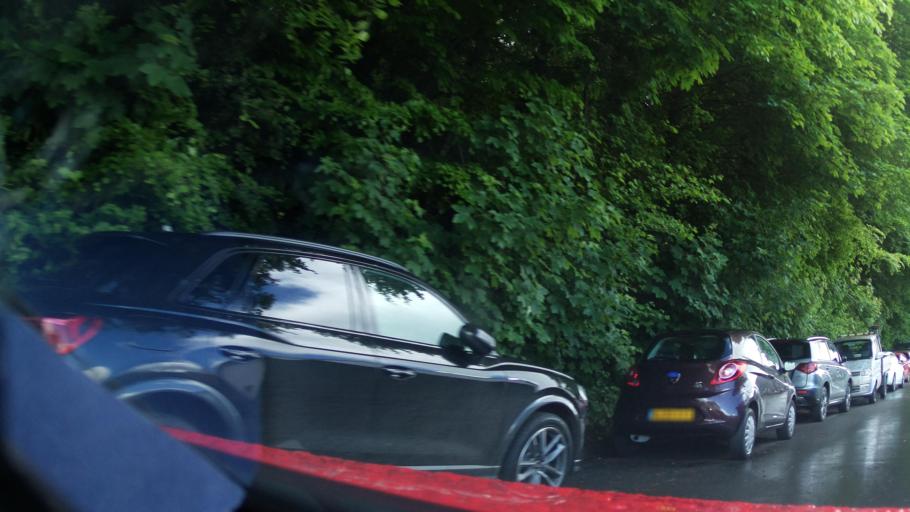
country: GB
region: England
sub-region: Devon
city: Dartmouth
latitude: 50.3503
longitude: -3.5662
